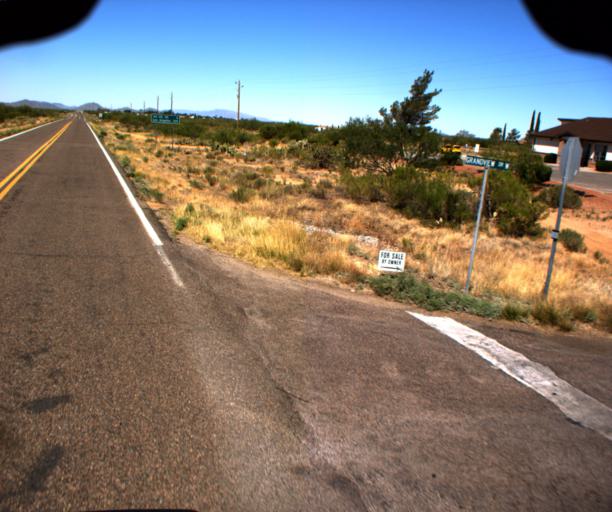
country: US
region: Arizona
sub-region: Yavapai County
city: Congress
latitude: 34.1611
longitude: -112.8557
